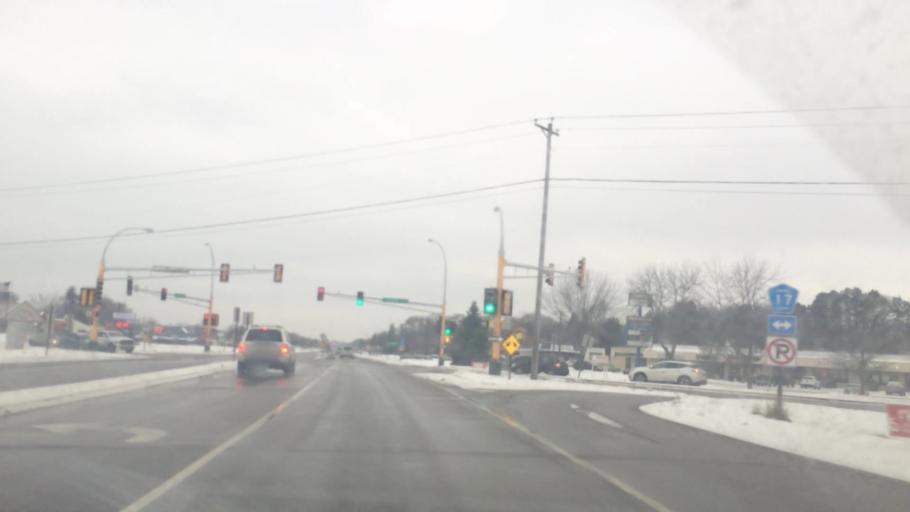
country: US
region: Minnesota
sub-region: Anoka County
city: Lexington
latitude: 45.1418
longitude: -93.1630
